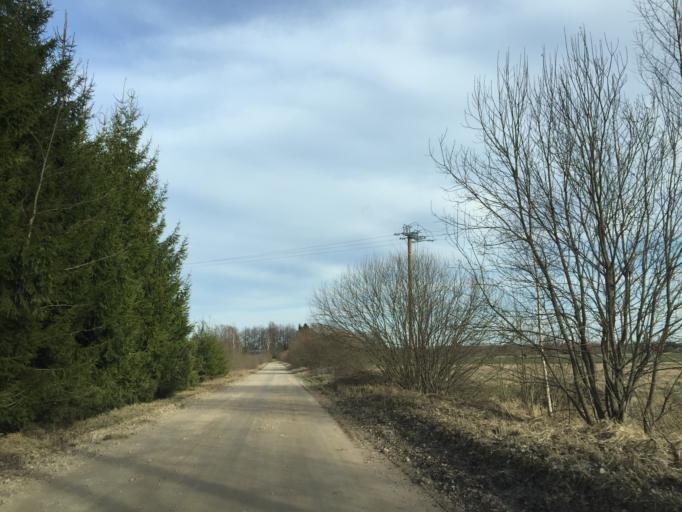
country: LV
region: Kegums
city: Kegums
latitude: 56.8072
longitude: 24.7824
